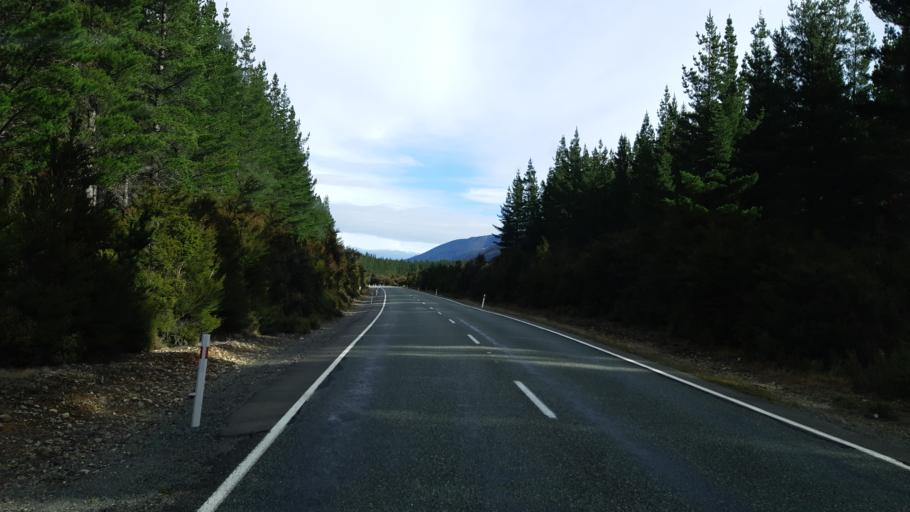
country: NZ
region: Tasman
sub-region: Tasman District
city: Wakefield
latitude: -41.7221
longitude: 173.0579
